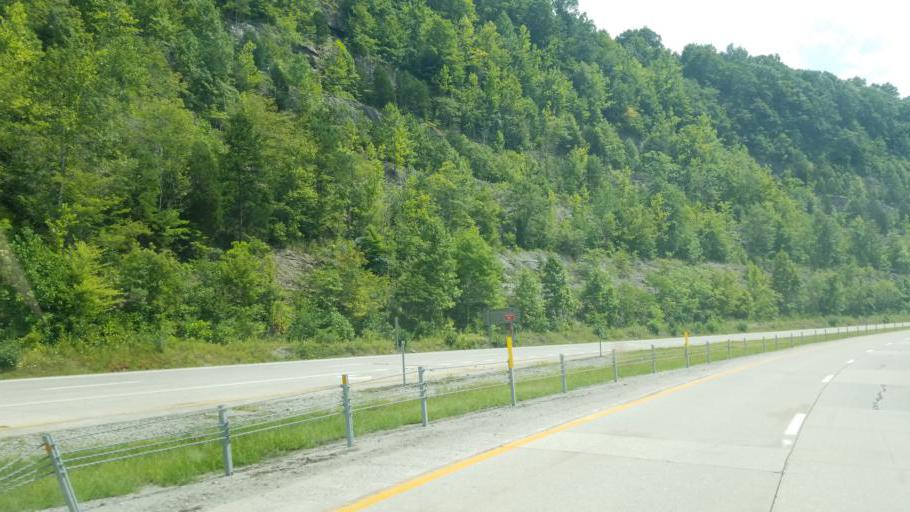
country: US
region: West Virginia
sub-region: Boone County
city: Madison
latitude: 38.1636
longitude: -81.8500
